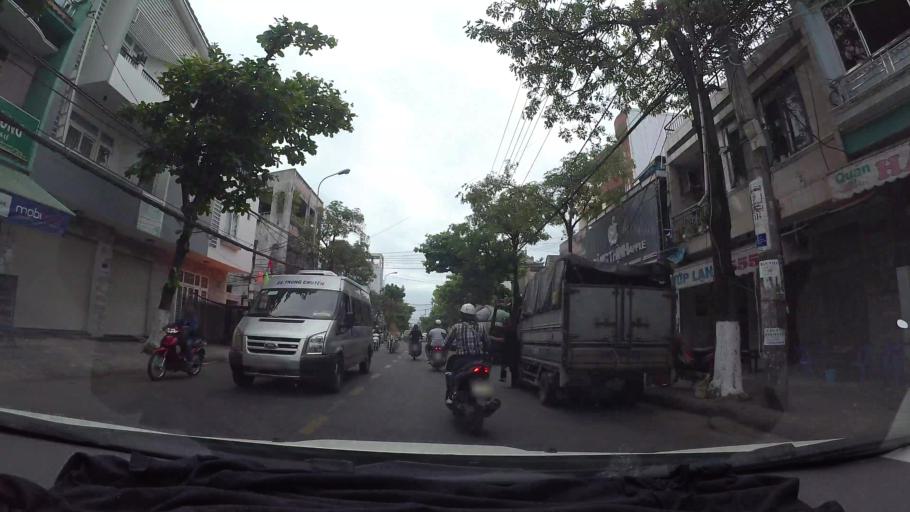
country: VN
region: Da Nang
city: Thanh Khe
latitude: 16.0713
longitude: 108.1888
